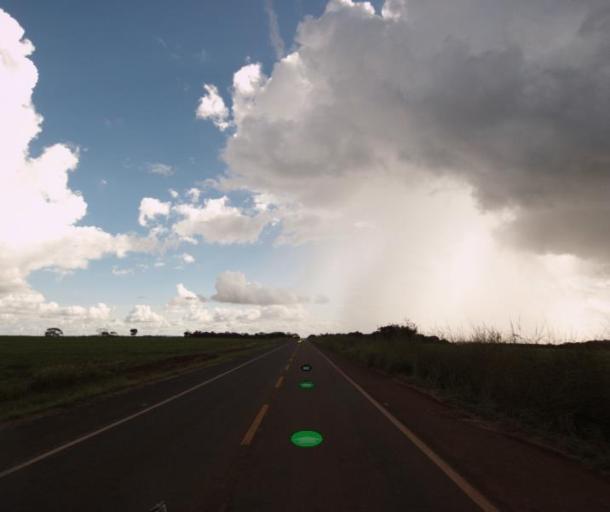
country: BR
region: Goias
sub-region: Itaberai
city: Itaberai
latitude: -15.9932
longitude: -49.7318
